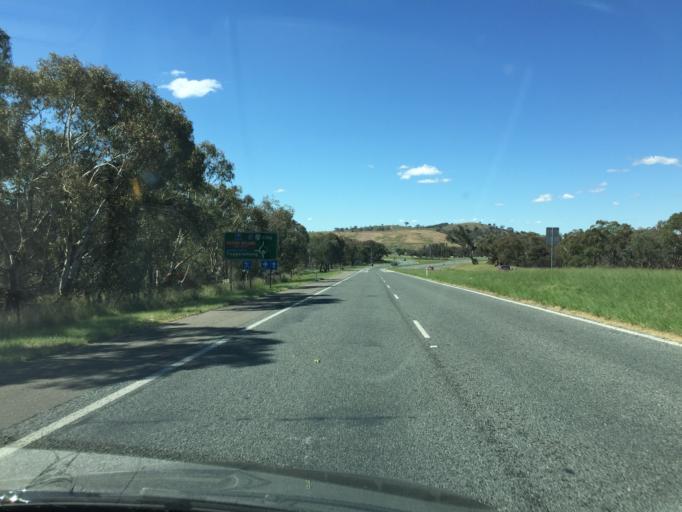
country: AU
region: Australian Capital Territory
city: Macarthur
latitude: -35.4095
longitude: 149.1446
